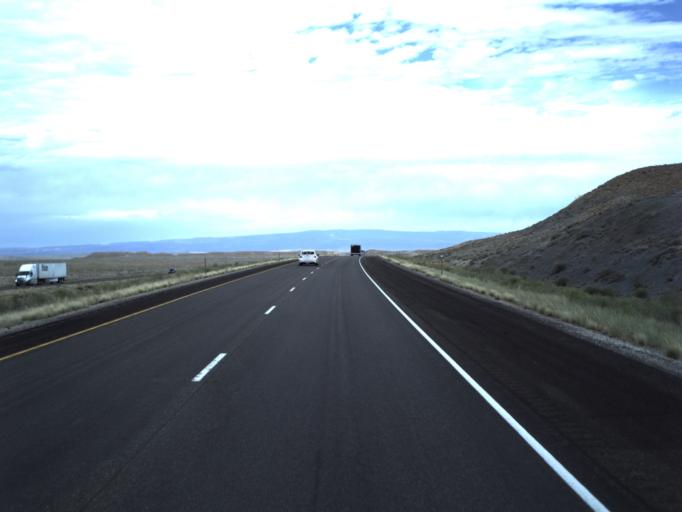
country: US
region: Utah
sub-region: Grand County
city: Moab
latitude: 38.9495
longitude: -109.6767
